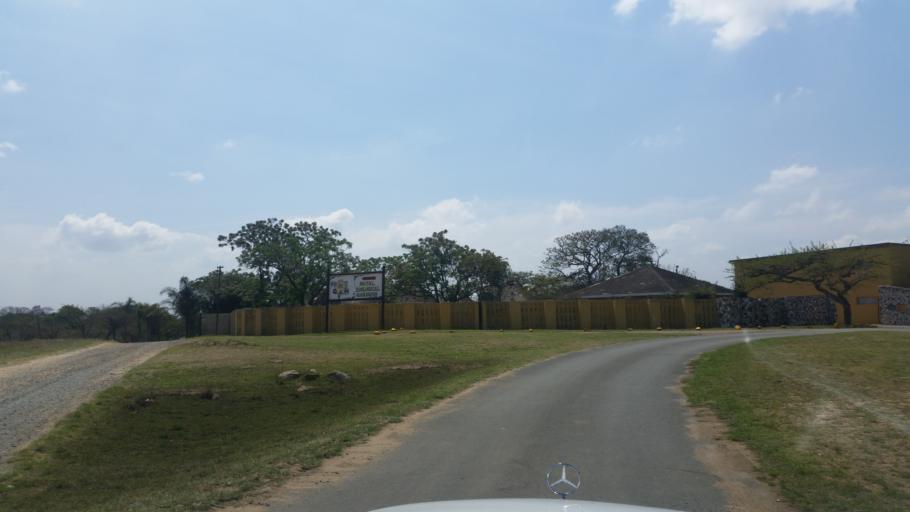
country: ZA
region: KwaZulu-Natal
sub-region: uMgungundlovu District Municipality
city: Camperdown
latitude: -29.6536
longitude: 30.5229
